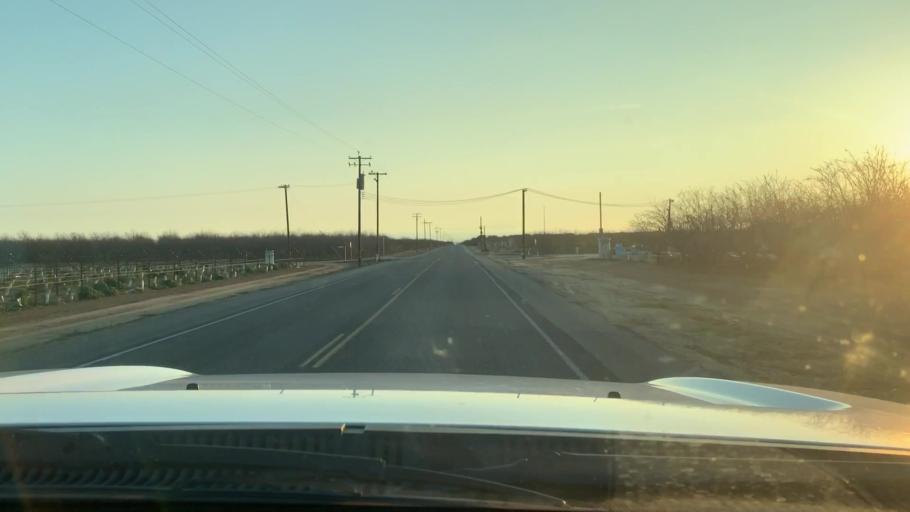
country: US
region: California
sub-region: Kern County
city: Buttonwillow
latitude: 35.5005
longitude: -119.4224
